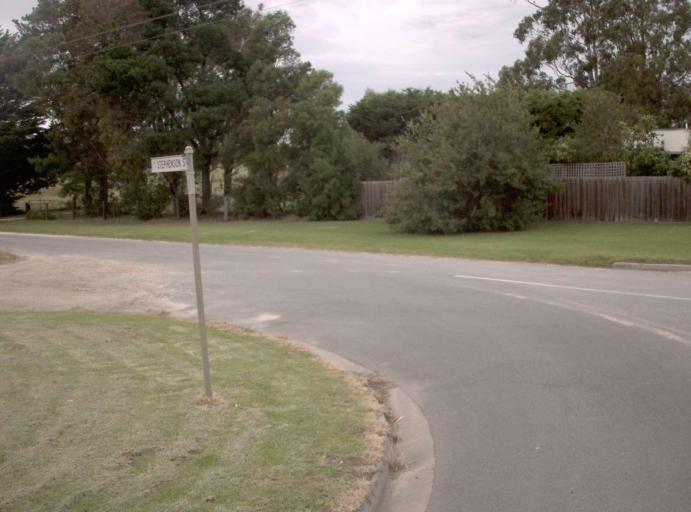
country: AU
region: Victoria
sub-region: Wellington
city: Sale
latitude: -38.1156
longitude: 147.0682
